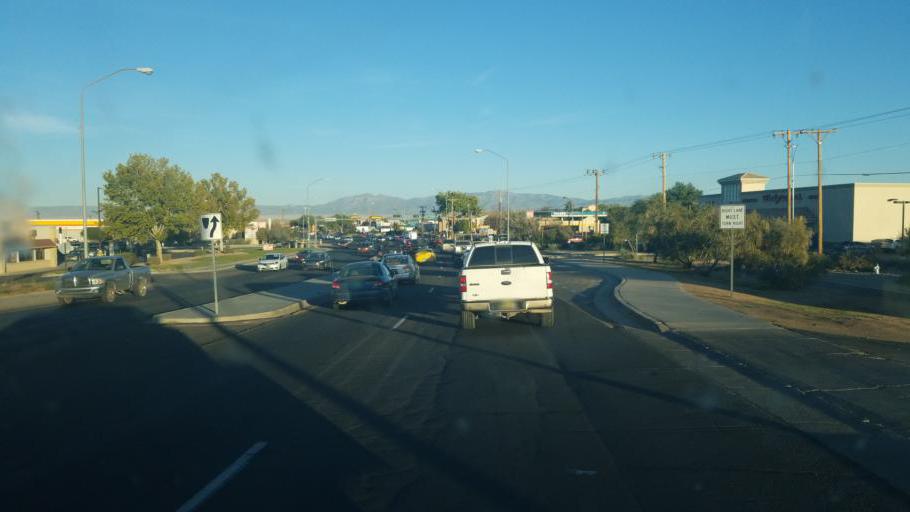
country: US
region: New Mexico
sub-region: Valencia County
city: Los Lunas
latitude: 34.8136
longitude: -106.7581
